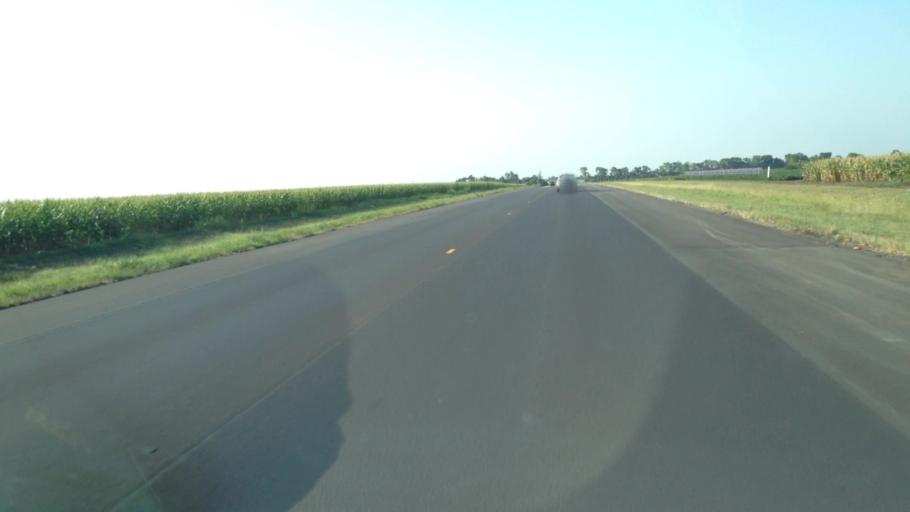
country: US
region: Kansas
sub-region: Anderson County
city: Garnett
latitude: 38.4423
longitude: -95.2487
